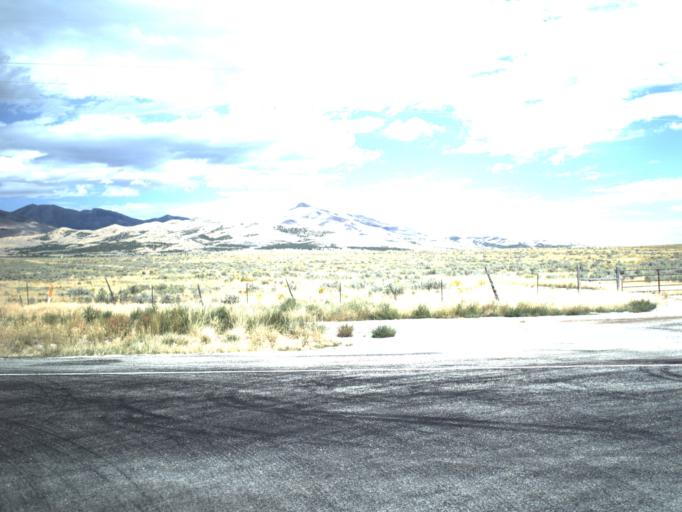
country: US
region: Idaho
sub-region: Oneida County
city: Malad City
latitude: 41.9651
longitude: -113.0610
